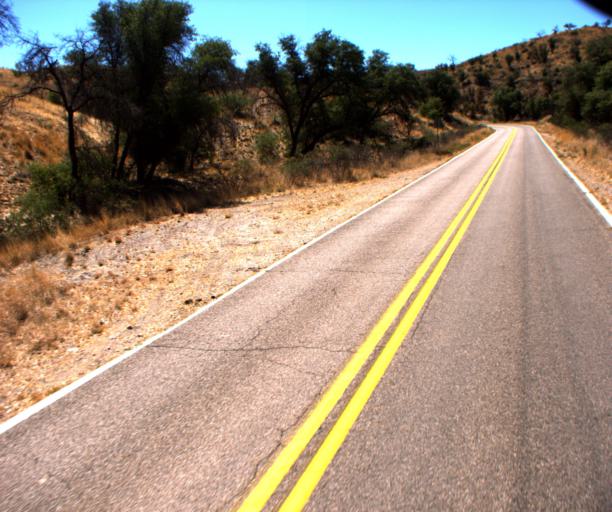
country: US
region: Arizona
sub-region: Santa Cruz County
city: Rio Rico
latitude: 31.3912
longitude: -111.0749
